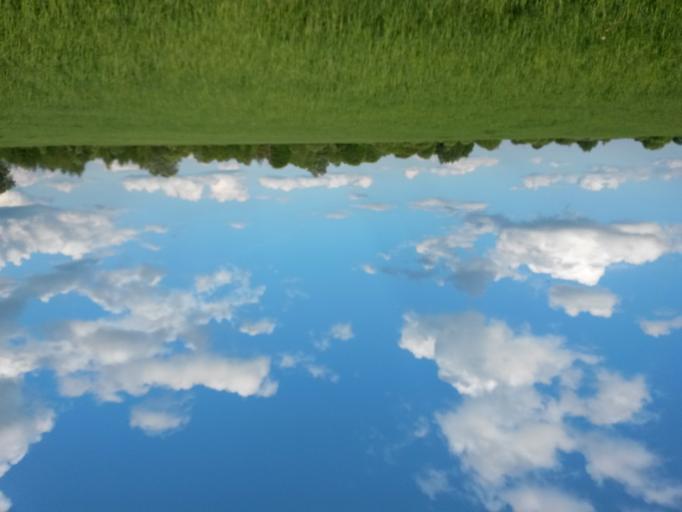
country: RU
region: Jaroslavl
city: Burmakino
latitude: 57.3631
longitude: 40.1990
